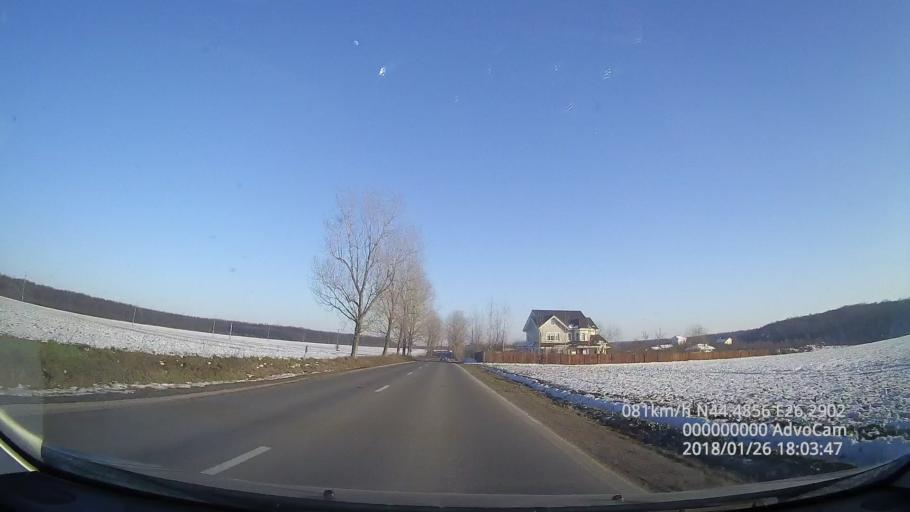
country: RO
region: Ilfov
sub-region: Comuna Ganeasa
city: Ganeasa
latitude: 44.4852
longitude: 26.2912
